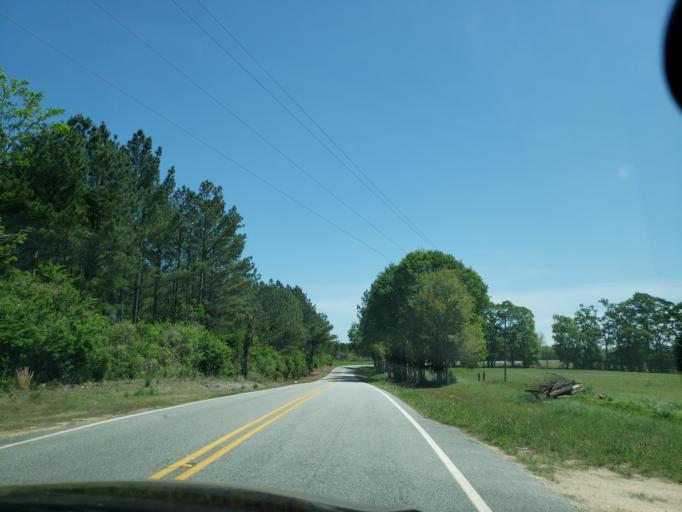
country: US
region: Alabama
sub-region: Tallapoosa County
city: Camp Hill
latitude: 32.7006
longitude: -85.6562
